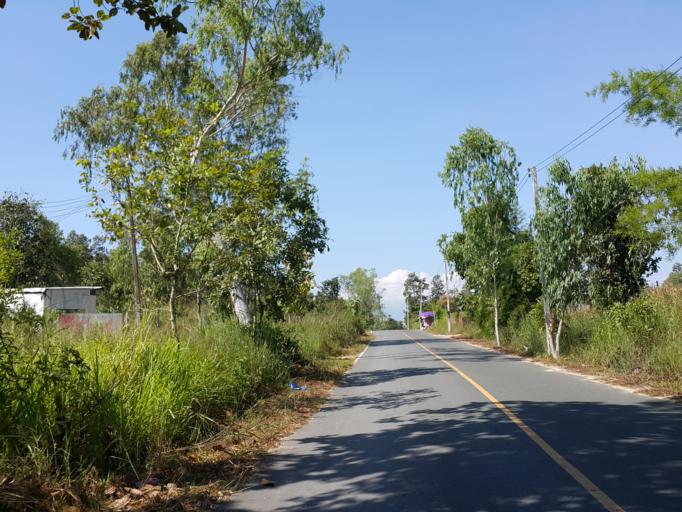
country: TH
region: Chiang Mai
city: San Sai
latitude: 18.8548
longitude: 99.1586
